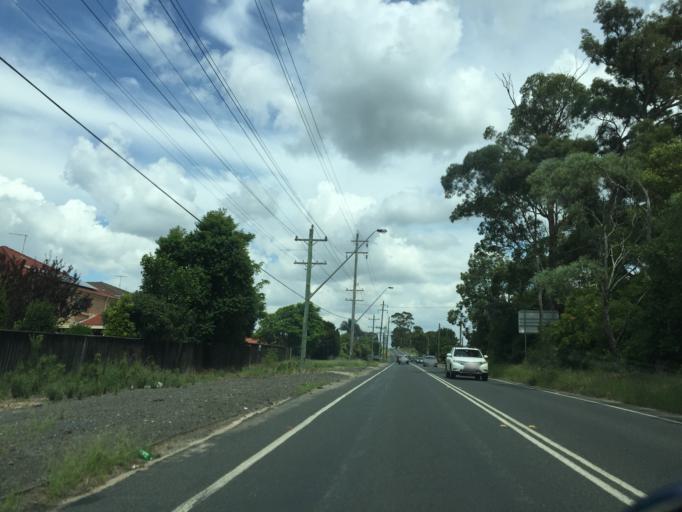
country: AU
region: New South Wales
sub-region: The Hills Shire
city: Beaumont Hills
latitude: -33.6972
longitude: 150.9666
